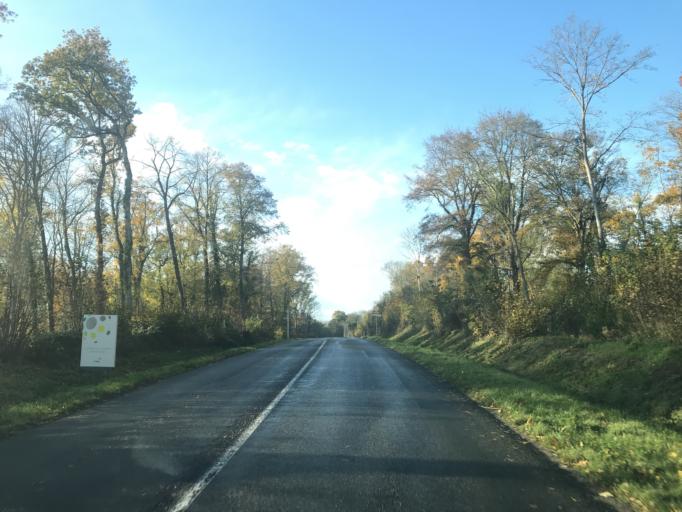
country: FR
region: Haute-Normandie
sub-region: Departement de l'Eure
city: Houlbec-Cocherel
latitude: 49.0823
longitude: 1.2974
